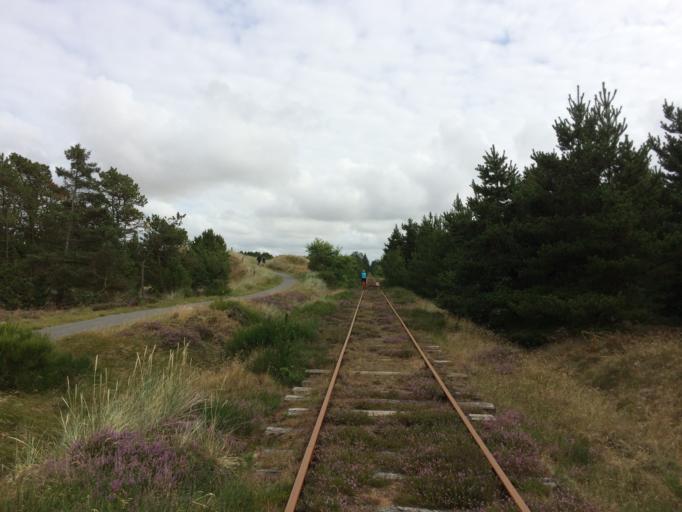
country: DK
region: South Denmark
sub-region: Varde Kommune
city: Oksbol
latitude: 55.8038
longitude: 8.2179
